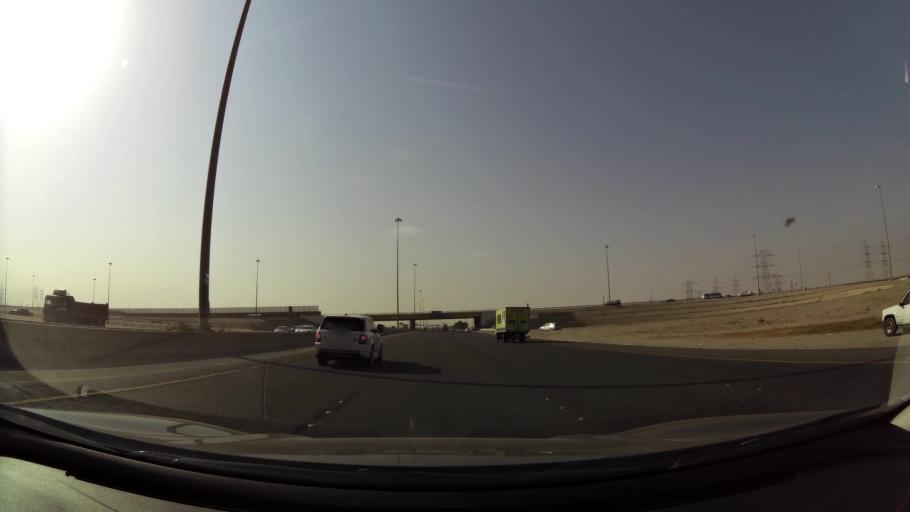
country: KW
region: Al Ahmadi
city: Al Ahmadi
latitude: 29.0650
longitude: 48.0983
